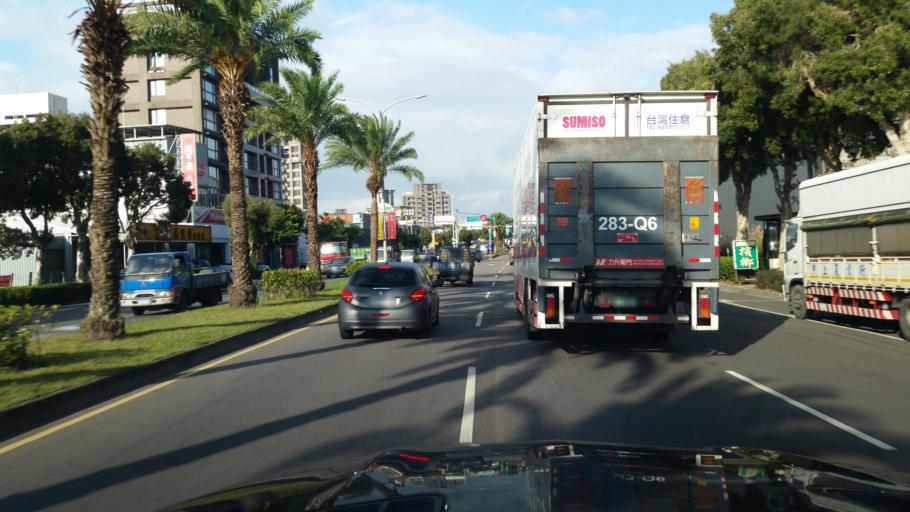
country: TW
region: Taiwan
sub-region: Taoyuan
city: Taoyuan
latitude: 25.0677
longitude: 121.3559
